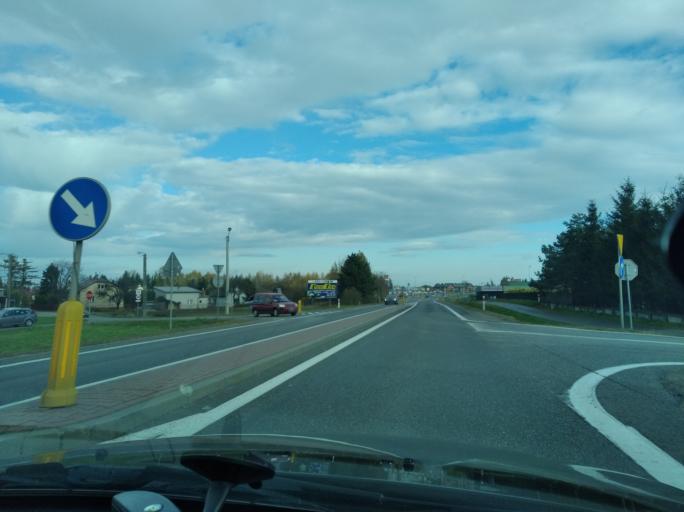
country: PL
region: Subcarpathian Voivodeship
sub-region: Powiat debicki
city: Debica
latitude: 50.0527
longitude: 21.4509
